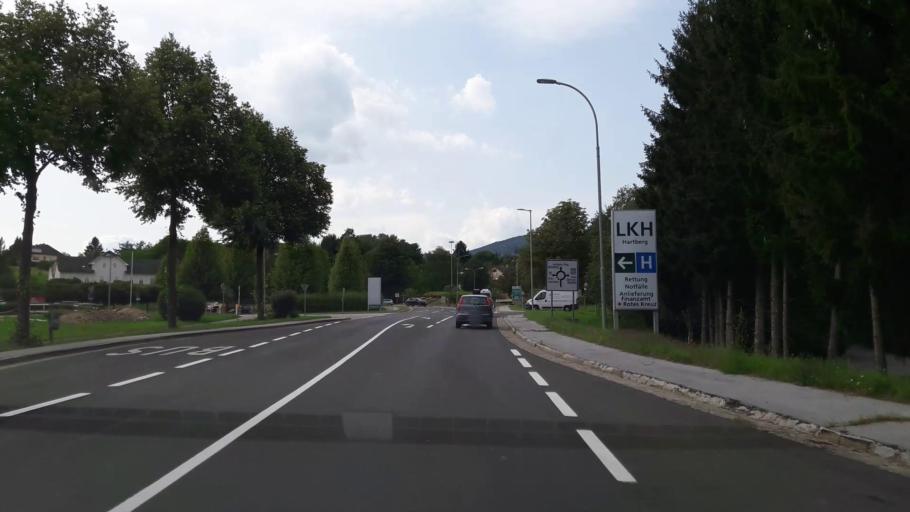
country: AT
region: Styria
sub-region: Politischer Bezirk Hartberg-Fuerstenfeld
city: Hartberg
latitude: 47.2738
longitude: 15.9664
